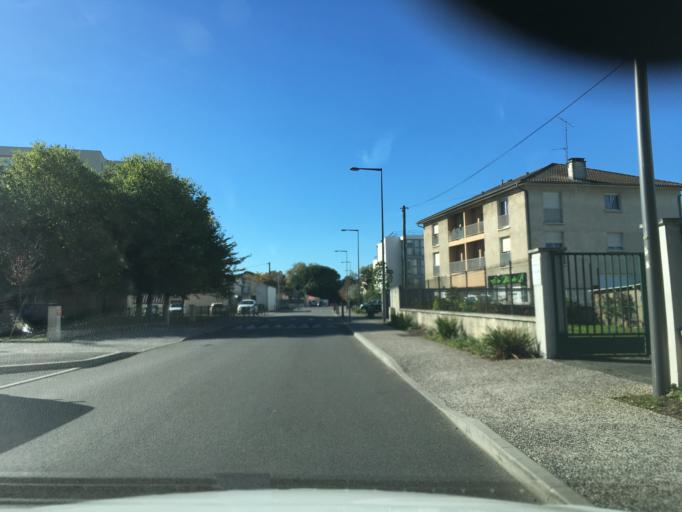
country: FR
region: Aquitaine
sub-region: Departement des Pyrenees-Atlantiques
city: Pau
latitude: 43.3172
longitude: -0.3473
